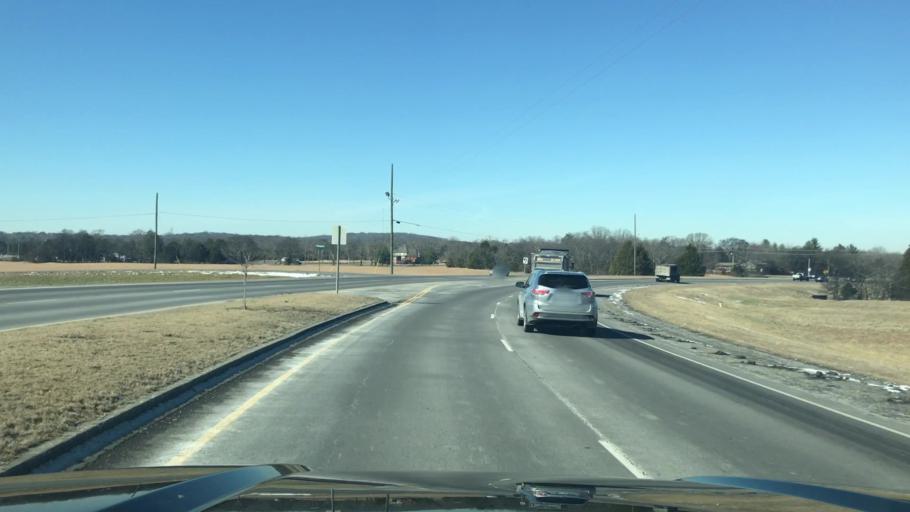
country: US
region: Tennessee
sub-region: Wilson County
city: Lebanon
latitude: 36.1926
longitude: -86.3307
